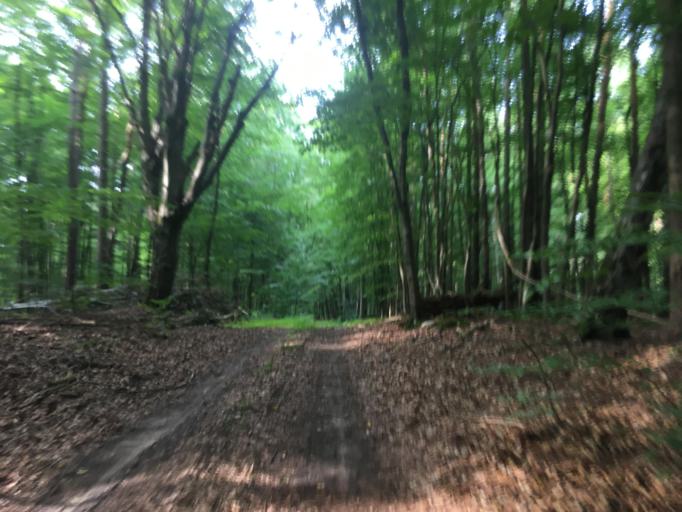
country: DE
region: Brandenburg
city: Eberswalde
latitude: 52.7954
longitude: 13.8211
